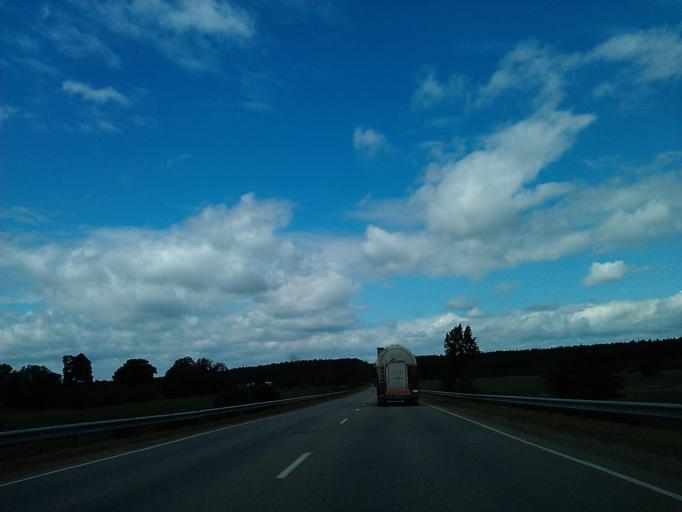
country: LV
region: Tukuma Rajons
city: Tukums
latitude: 56.9407
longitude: 23.1651
